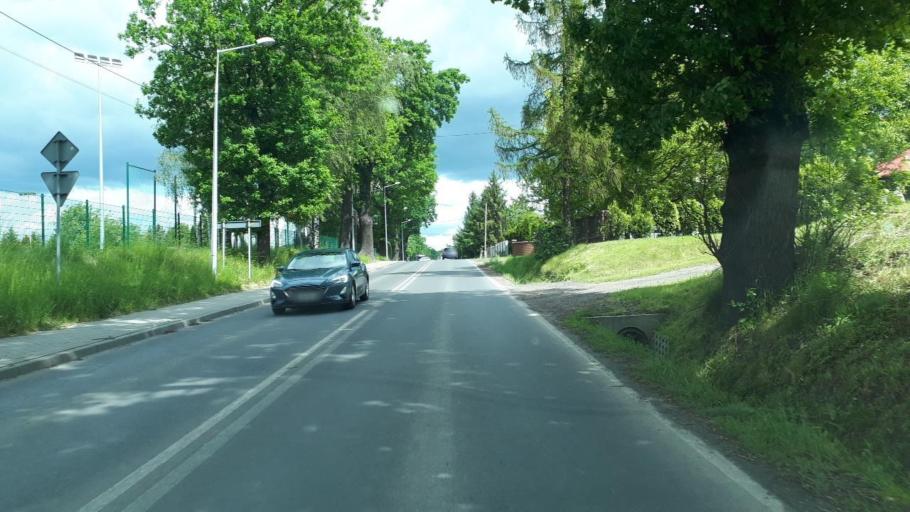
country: PL
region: Lesser Poland Voivodeship
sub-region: Powiat oswiecimski
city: Brzeszcze
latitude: 49.9624
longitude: 19.1389
